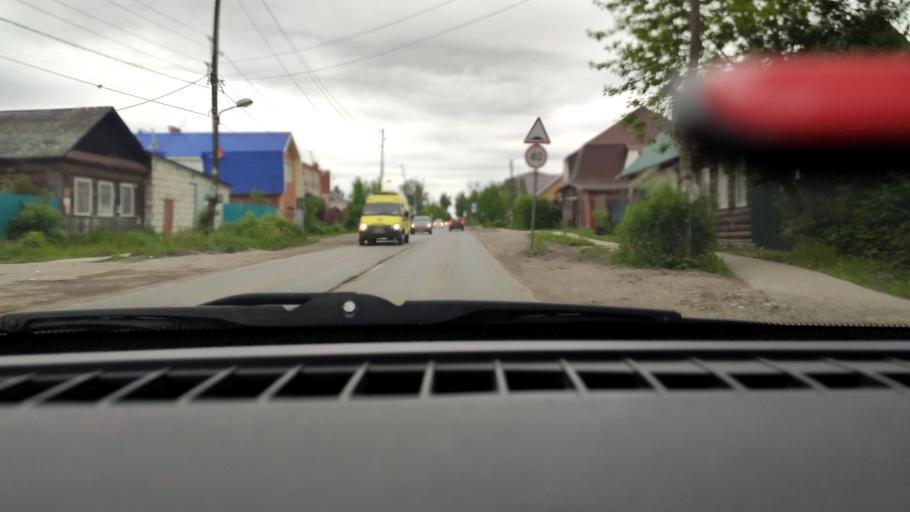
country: RU
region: Perm
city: Perm
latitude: 58.0437
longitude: 56.3289
